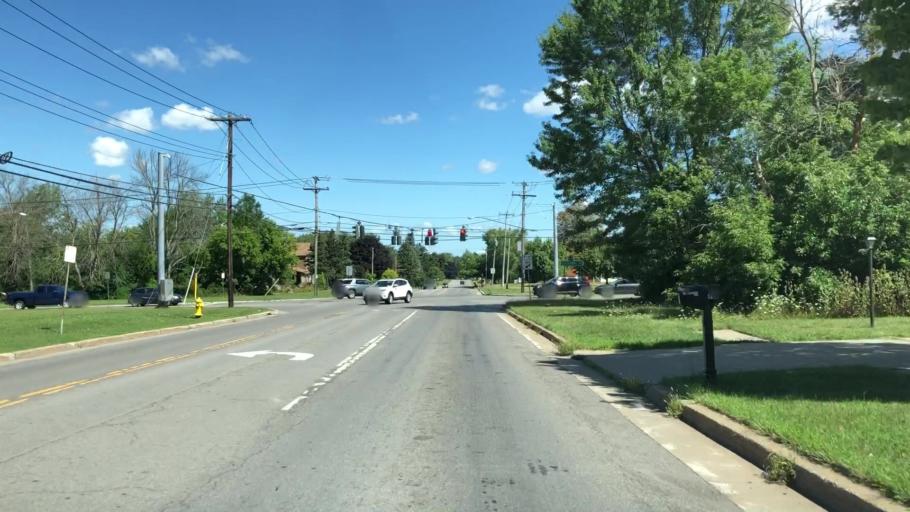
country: US
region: New York
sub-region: Erie County
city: Depew
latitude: 42.8795
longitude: -78.7089
